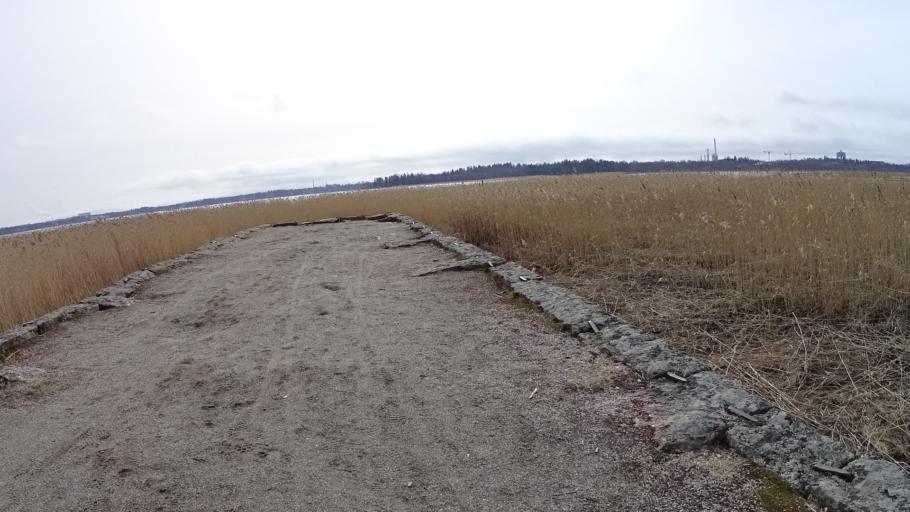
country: FI
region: Uusimaa
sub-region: Helsinki
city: Teekkarikylae
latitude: 60.2001
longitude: 24.8246
